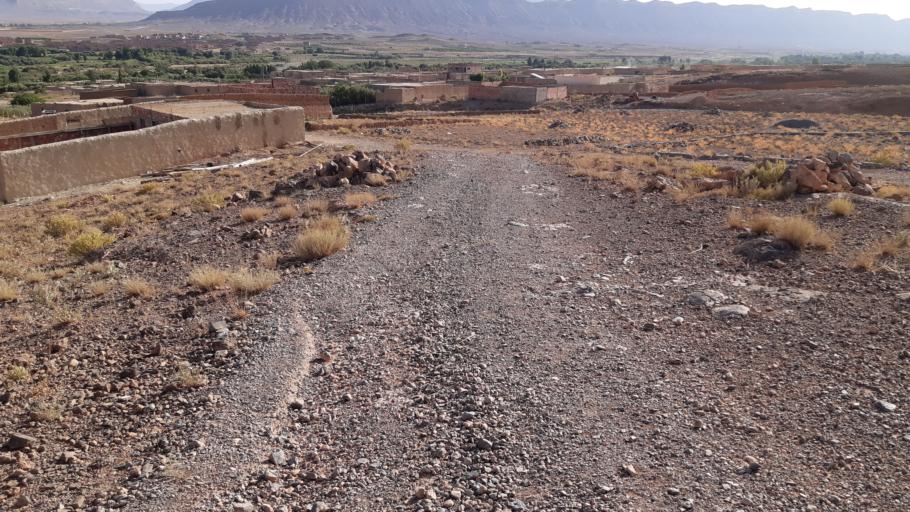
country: MA
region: Meknes-Tafilalet
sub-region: Errachidia
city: Errachidia
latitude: 32.2457
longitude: -4.4847
